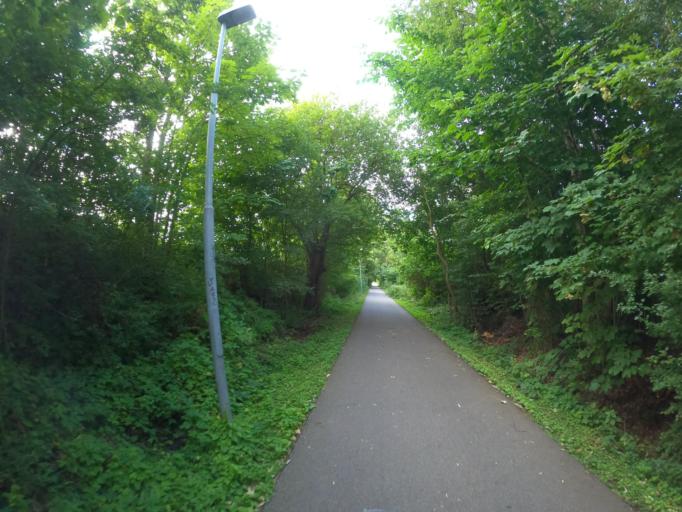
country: SE
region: Skane
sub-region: Lunds Kommun
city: Lund
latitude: 55.6849
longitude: 13.1898
